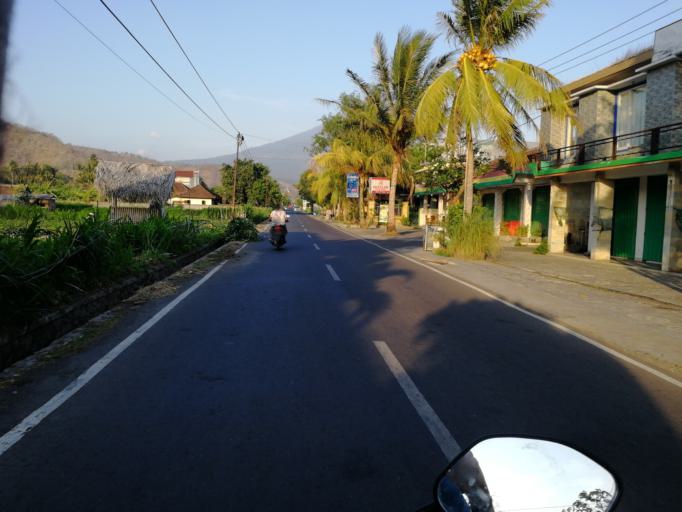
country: ID
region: Bali
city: Biaslantang Kaler
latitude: -8.3339
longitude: 115.6399
